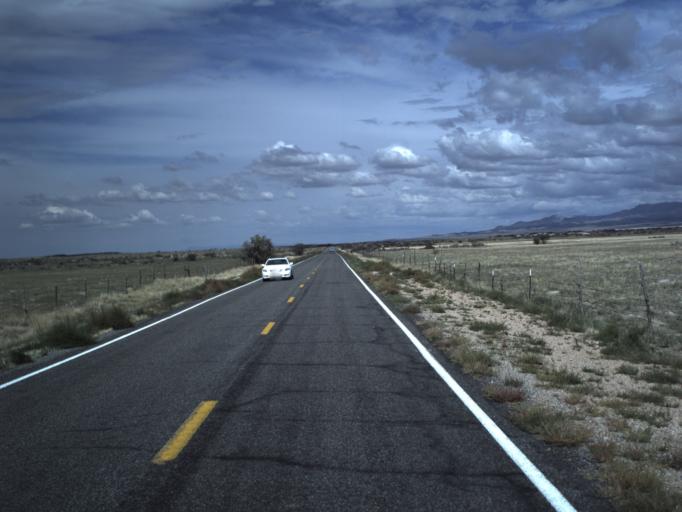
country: US
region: Utah
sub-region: Millard County
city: Fillmore
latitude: 39.1038
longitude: -112.4100
